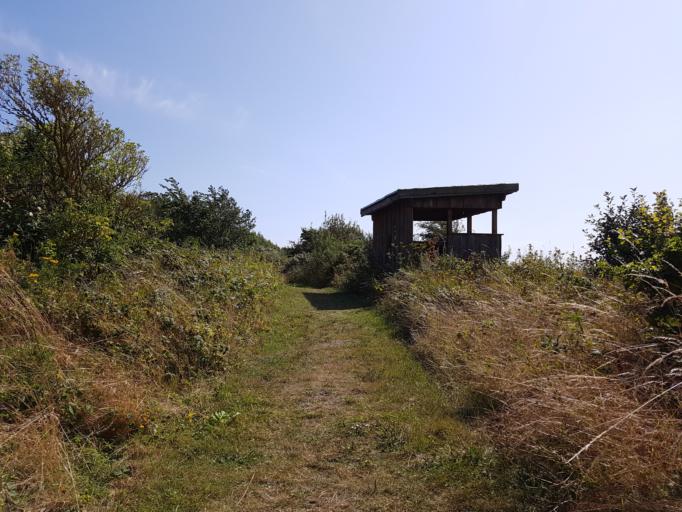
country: DK
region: Zealand
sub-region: Guldborgsund Kommune
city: Nykobing Falster
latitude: 54.5768
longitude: 11.9218
